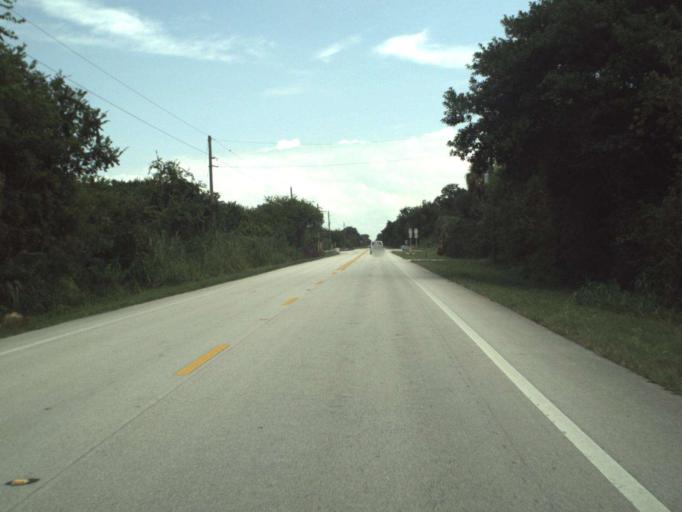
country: US
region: Florida
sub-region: Martin County
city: Indiantown
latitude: 27.0099
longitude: -80.6256
